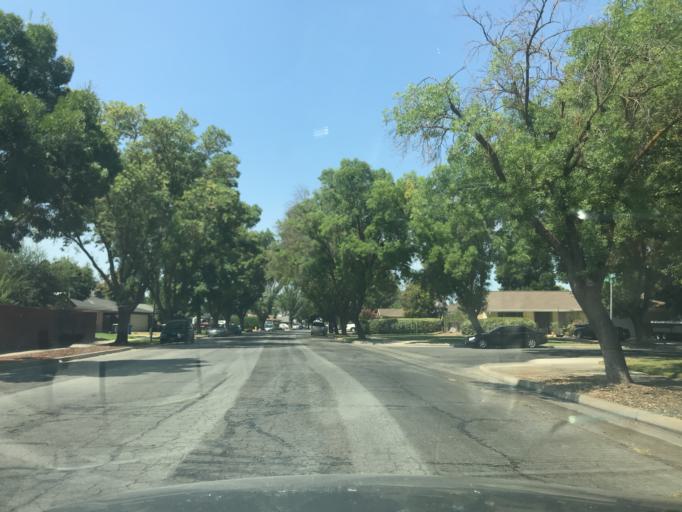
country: US
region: California
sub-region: Merced County
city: Merced
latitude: 37.3297
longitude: -120.4821
